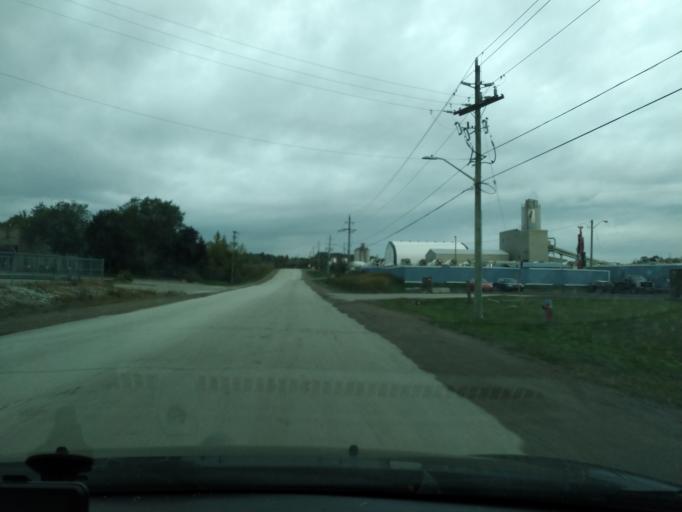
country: CA
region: Ontario
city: Bradford West Gwillimbury
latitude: 44.1375
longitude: -79.5555
